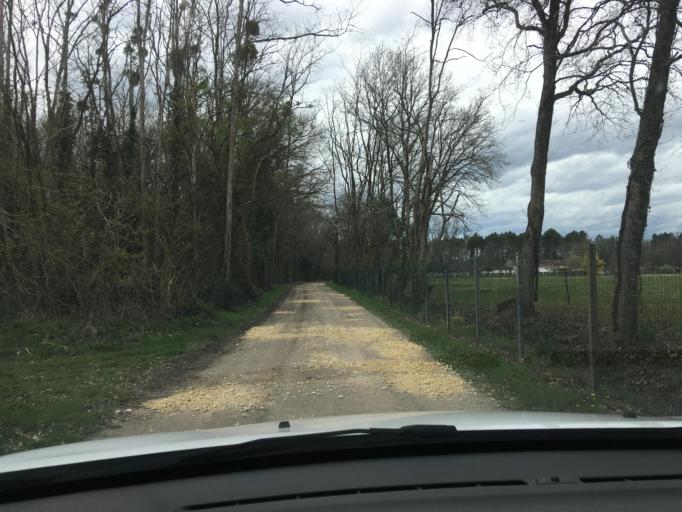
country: FR
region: Aquitaine
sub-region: Departement de la Gironde
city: Saint-Sauveur
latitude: 45.2227
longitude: -0.8687
